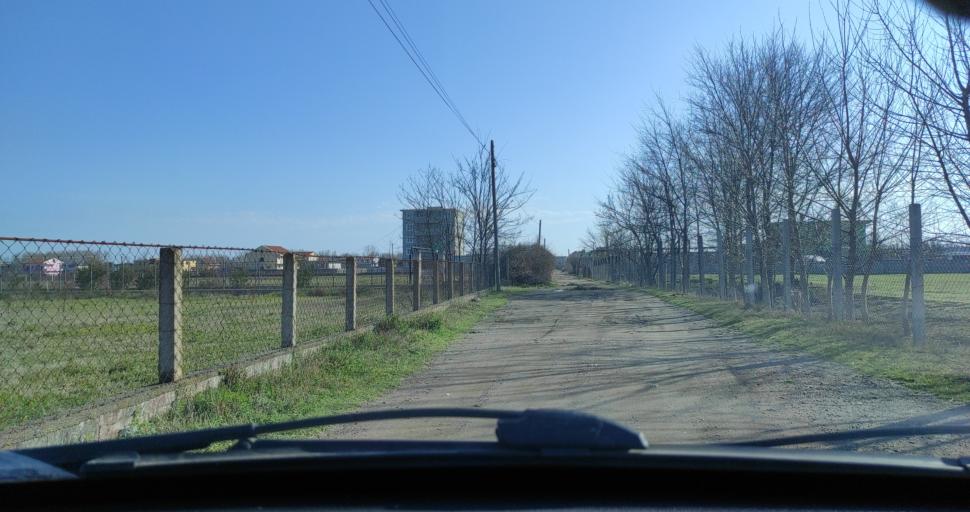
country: AL
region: Shkoder
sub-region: Rrethi i Shkodres
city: Velipoje
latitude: 41.8717
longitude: 19.4114
